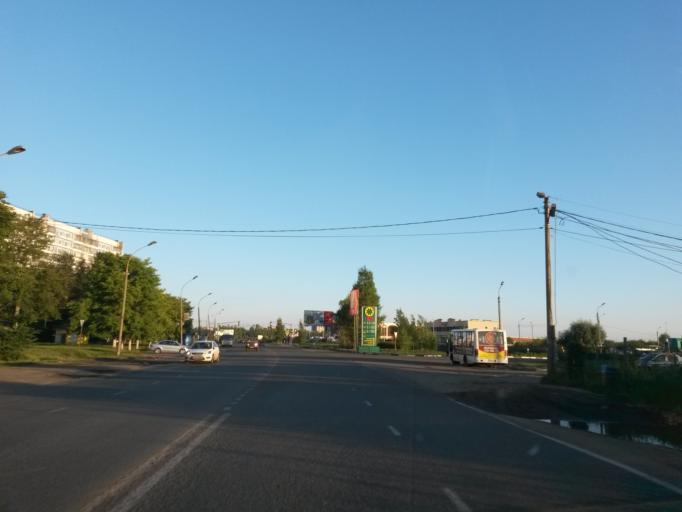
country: RU
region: Jaroslavl
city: Yaroslavl
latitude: 57.7030
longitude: 39.7593
